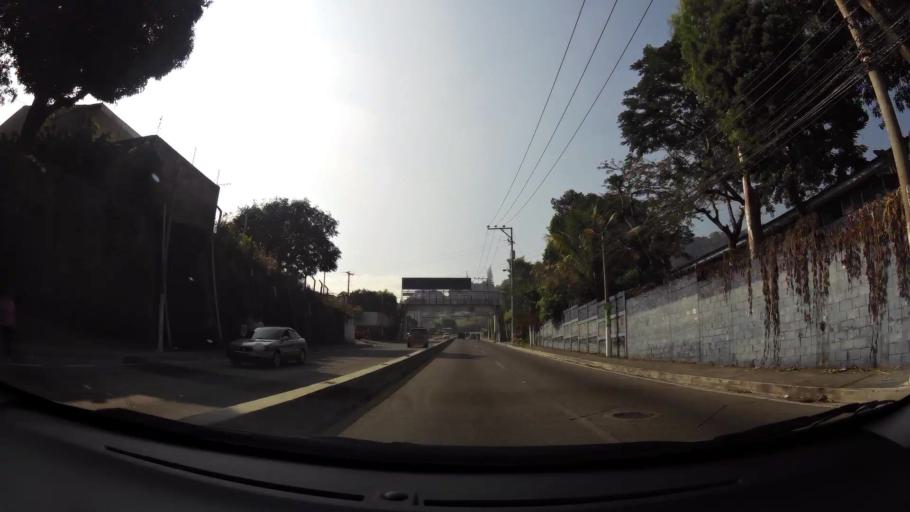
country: SV
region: La Libertad
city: Antiguo Cuscatlan
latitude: 13.6682
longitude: -89.2234
